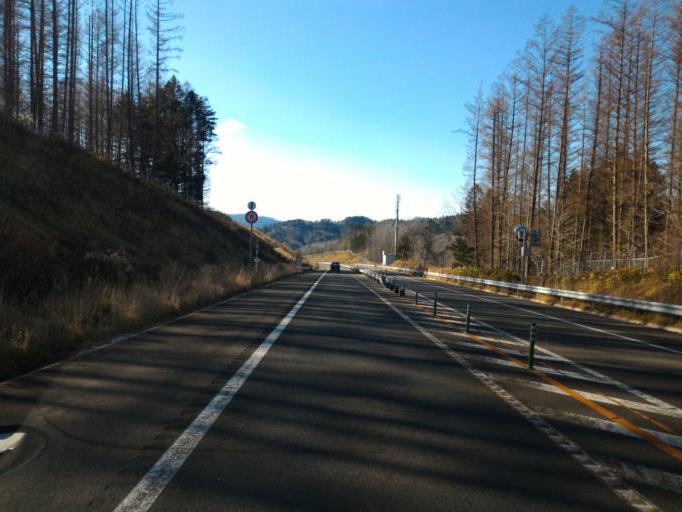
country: JP
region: Hokkaido
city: Shimo-furano
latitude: 42.9428
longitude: 142.2186
